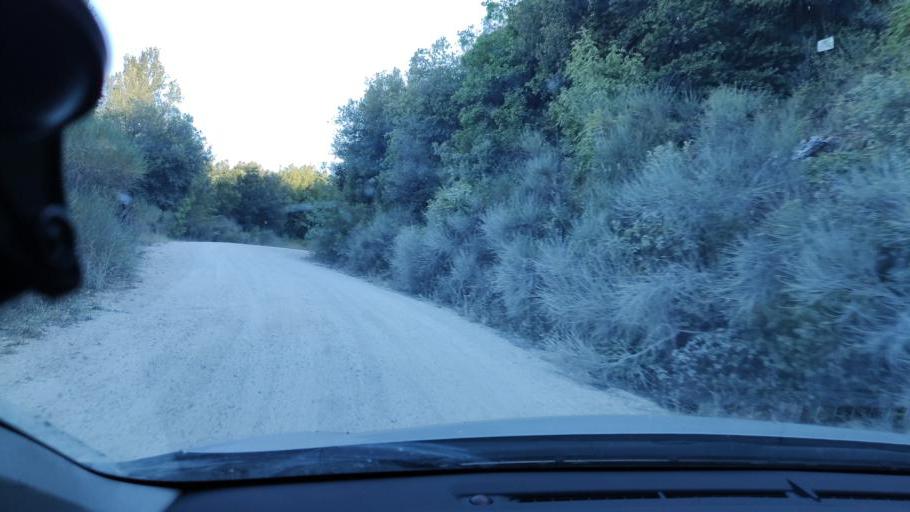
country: IT
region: Umbria
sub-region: Provincia di Terni
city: Amelia
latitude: 42.5378
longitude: 12.3818
